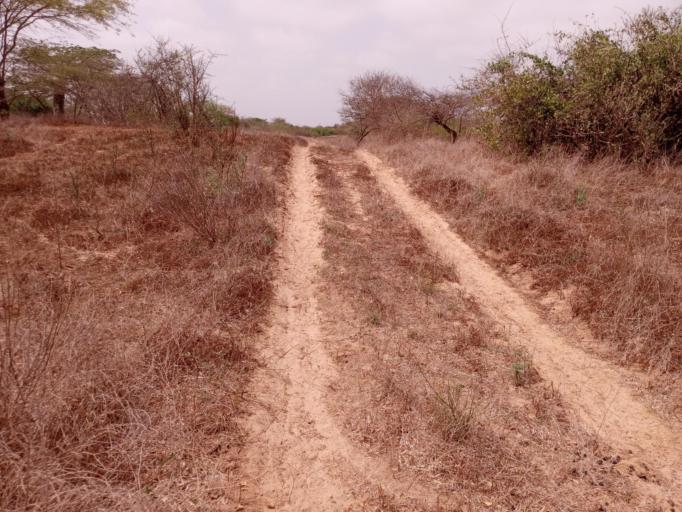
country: SN
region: Saint-Louis
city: Saint-Louis
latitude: 15.9153
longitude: -16.4540
